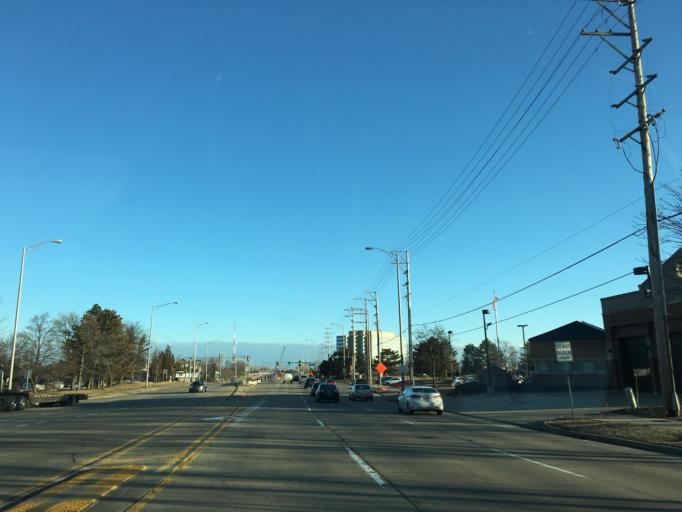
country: US
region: Illinois
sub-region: Cook County
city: Hoffman Estates
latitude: 42.0564
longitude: -88.0796
